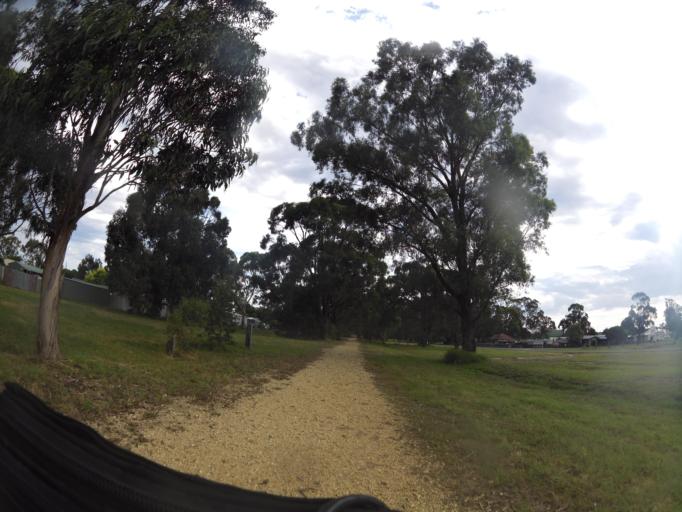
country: AU
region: Victoria
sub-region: Latrobe
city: Traralgon
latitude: -38.0572
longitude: 146.6272
